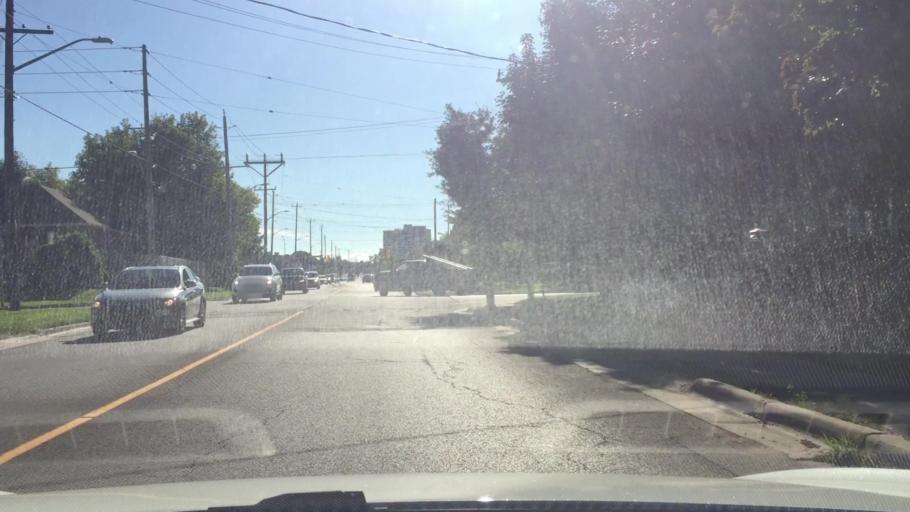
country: CA
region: Ontario
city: Oshawa
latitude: 43.9070
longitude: -78.8542
